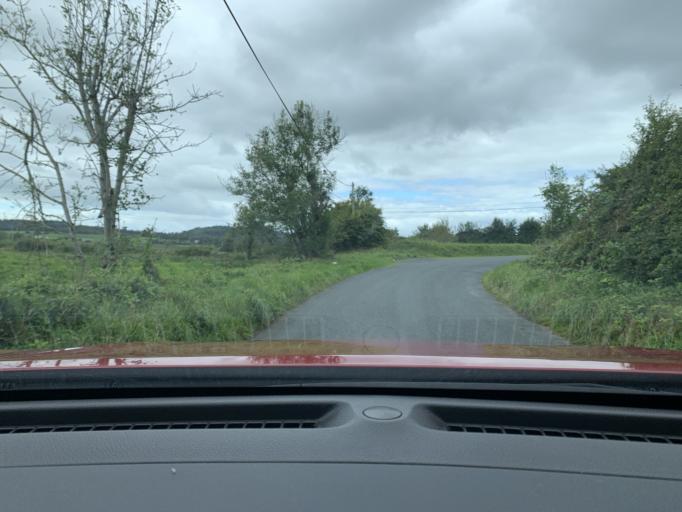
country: IE
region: Connaught
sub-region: Sligo
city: Collooney
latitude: 54.1883
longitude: -8.4527
